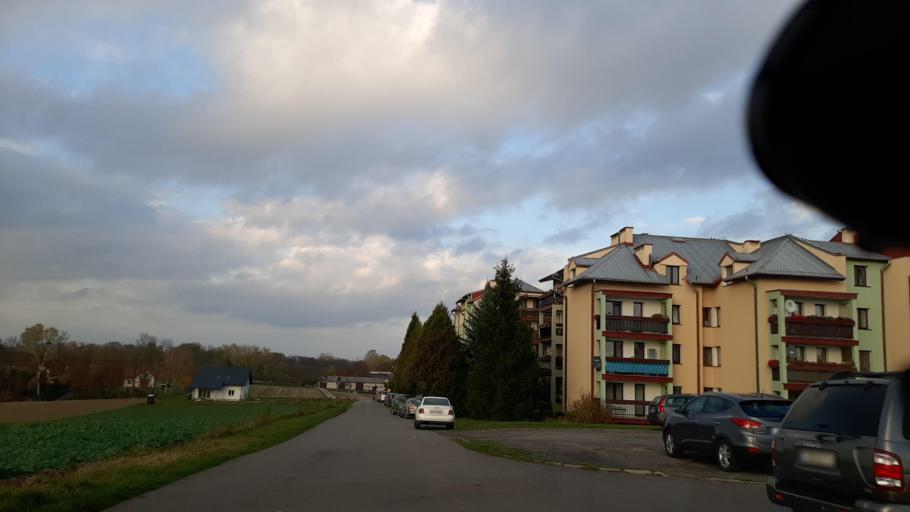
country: PL
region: Lublin Voivodeship
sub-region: Powiat lubelski
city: Garbow
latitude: 51.3473
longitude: 22.3301
